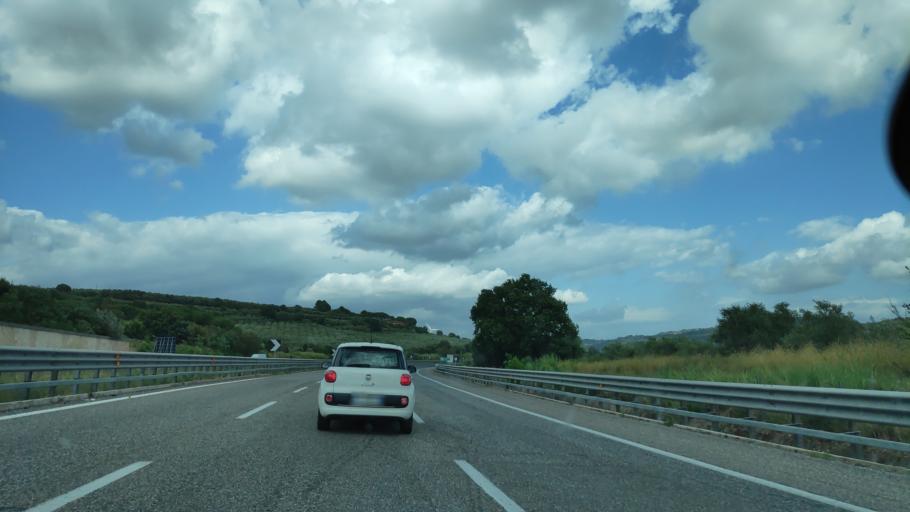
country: IT
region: Campania
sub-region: Provincia di Salerno
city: Quadrivio
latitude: 40.6128
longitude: 15.1404
